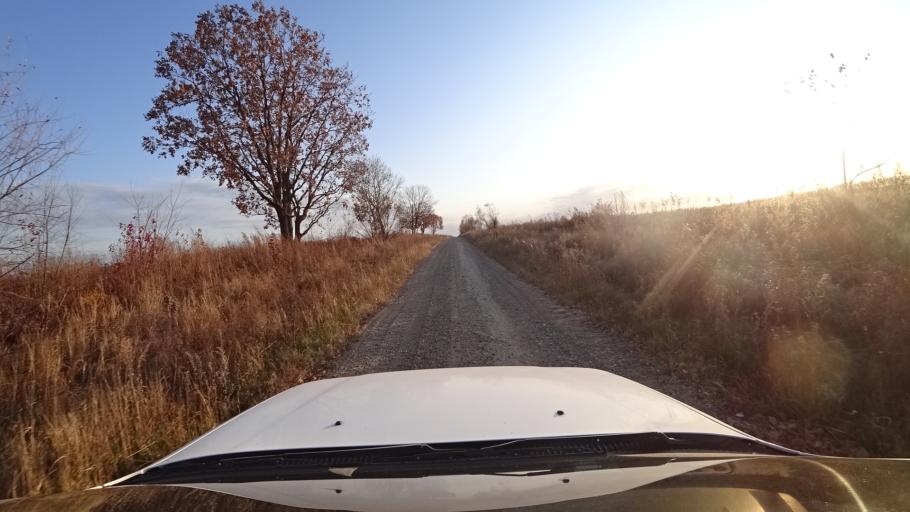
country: RU
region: Primorskiy
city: Lazo
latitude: 45.8138
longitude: 133.6098
